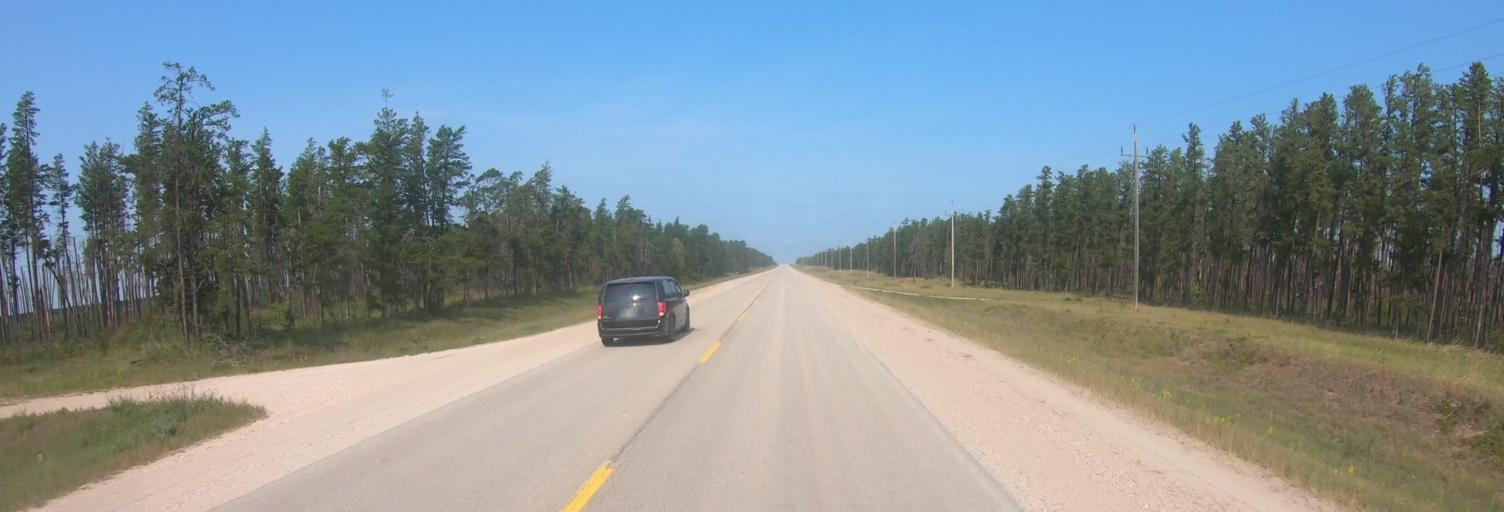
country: US
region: Minnesota
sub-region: Roseau County
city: Roseau
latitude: 49.1256
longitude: -96.0683
